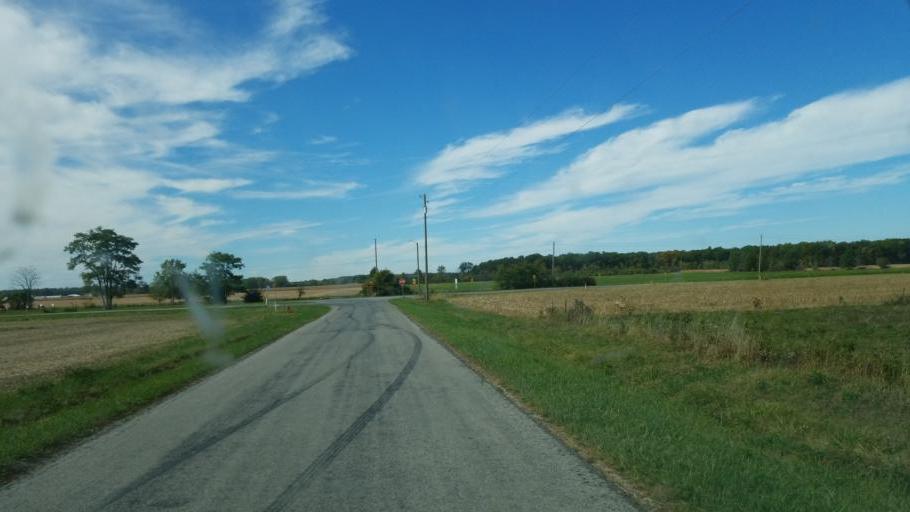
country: US
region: Ohio
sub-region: Huron County
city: Wakeman
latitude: 41.2848
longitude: -82.4906
